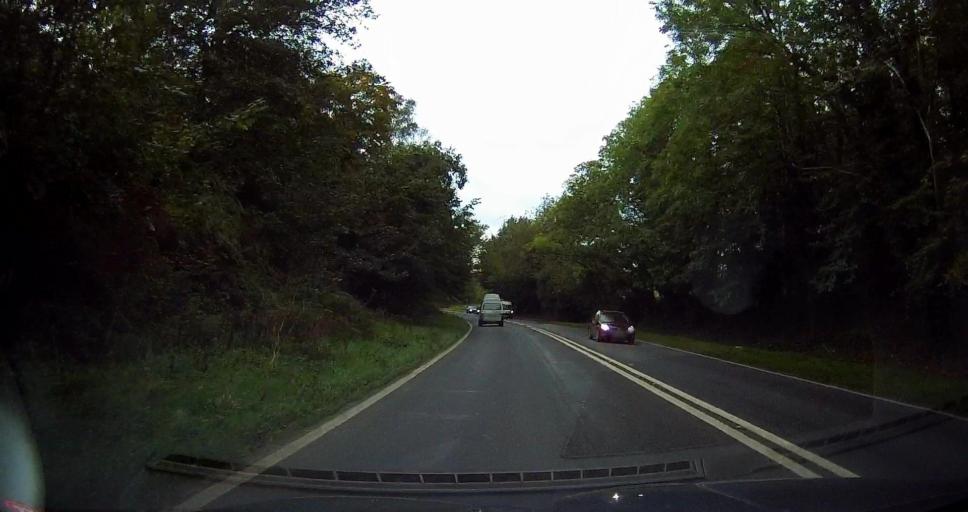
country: GB
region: England
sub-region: Kent
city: Harrietsham
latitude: 51.2546
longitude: 0.6306
